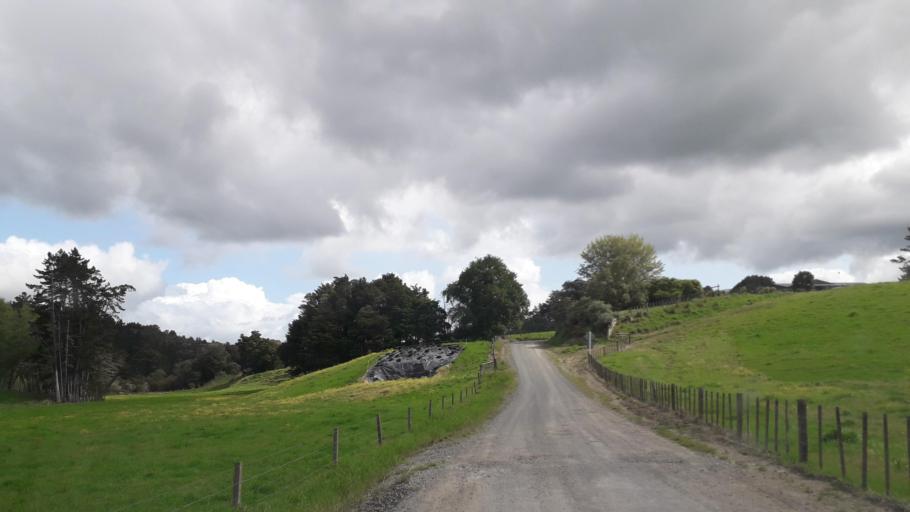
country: NZ
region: Northland
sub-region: Far North District
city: Waimate North
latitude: -35.2990
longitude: 173.5658
